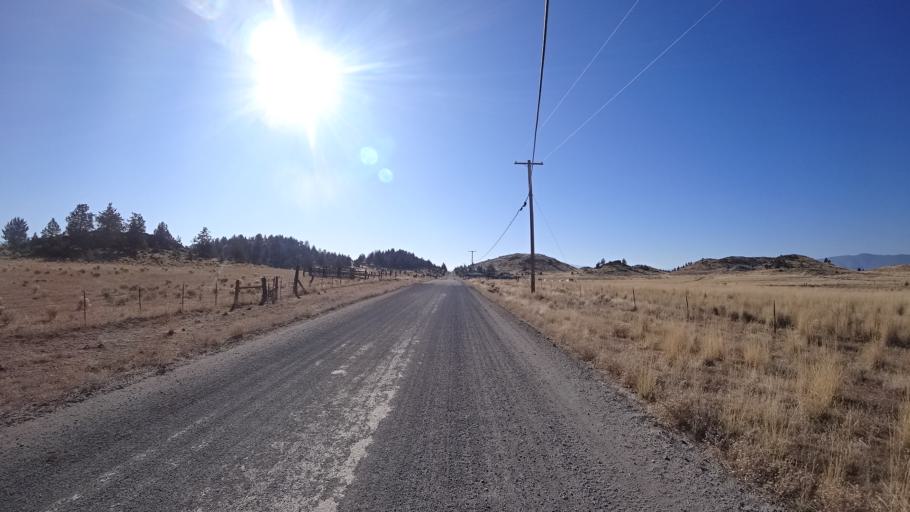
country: US
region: California
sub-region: Siskiyou County
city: Montague
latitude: 41.7036
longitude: -122.4377
